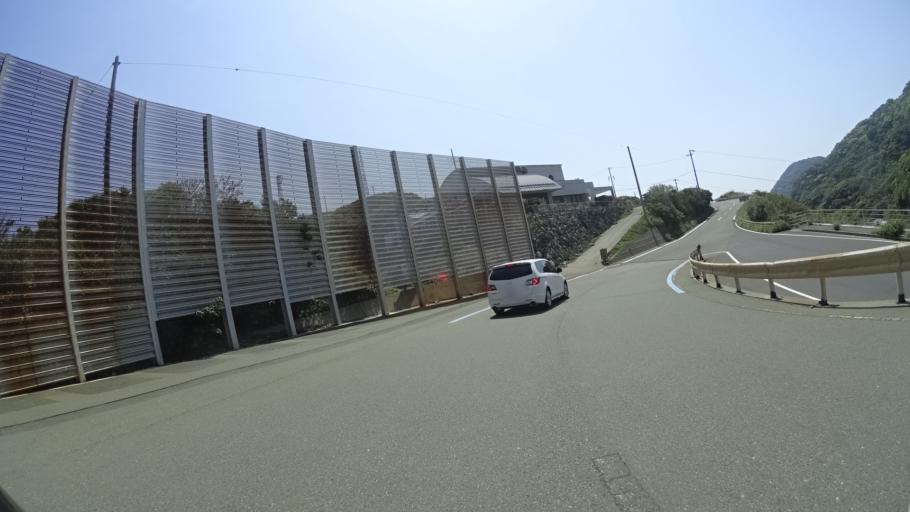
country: JP
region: Ehime
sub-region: Nishiuwa-gun
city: Ikata-cho
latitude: 33.3675
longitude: 132.0443
